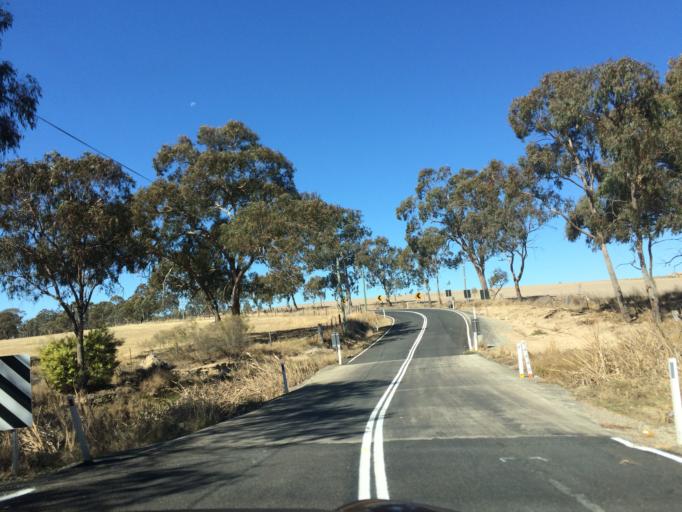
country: AU
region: Queensland
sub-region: Southern Downs
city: Stanthorpe
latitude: -28.6958
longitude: 152.0080
